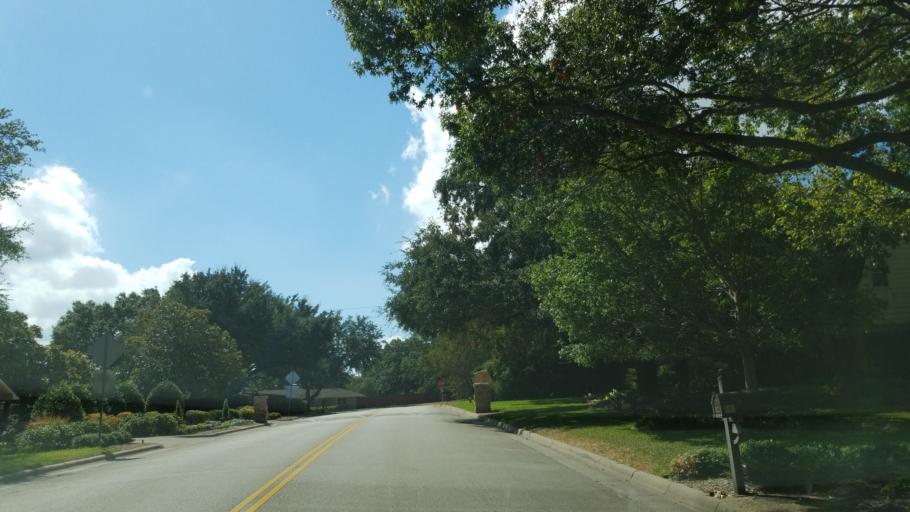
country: US
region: Texas
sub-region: Dallas County
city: Addison
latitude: 32.9341
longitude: -96.7981
